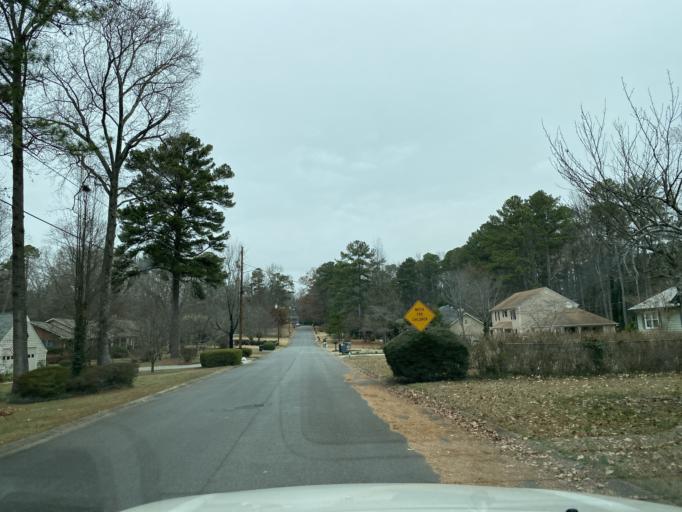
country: US
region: Georgia
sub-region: Cobb County
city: Fair Oaks
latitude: 33.9215
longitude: -84.5684
